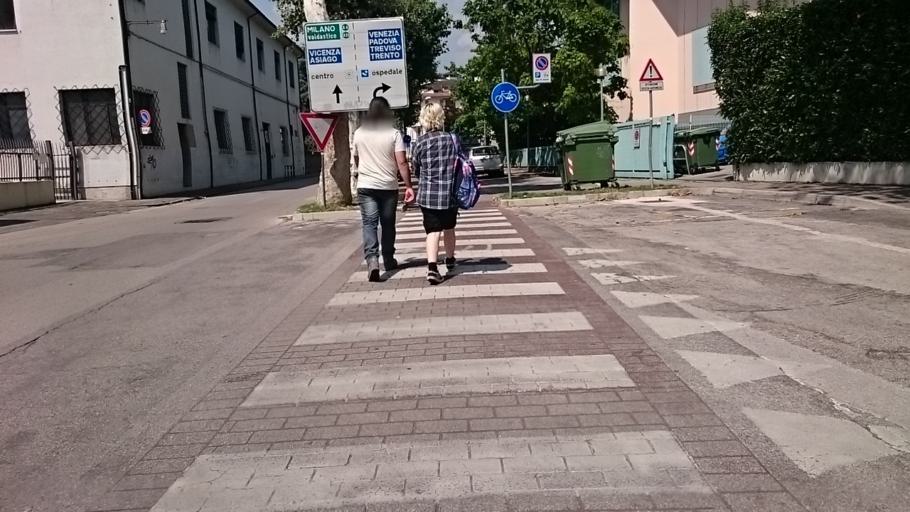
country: IT
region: Veneto
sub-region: Provincia di Vicenza
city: Bassano del Grappa
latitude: 45.7622
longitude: 11.7347
